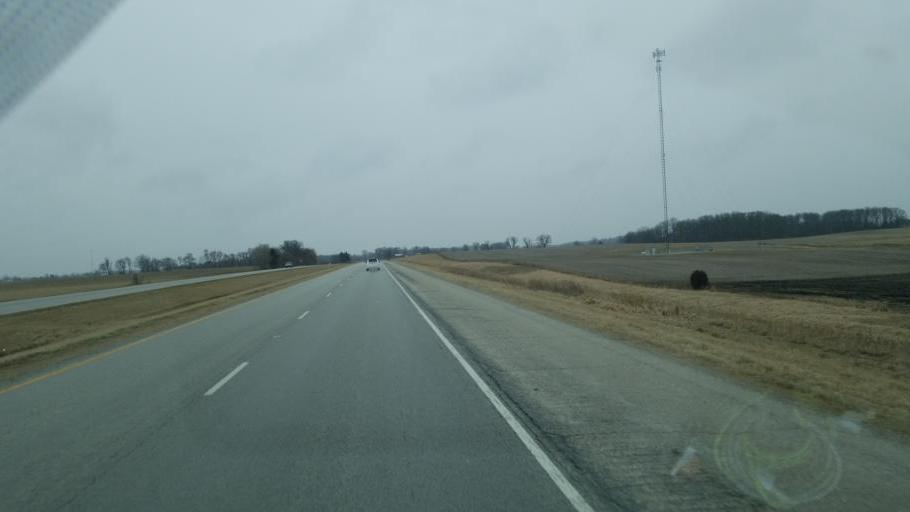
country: US
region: Indiana
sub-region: Fulton County
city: Rochester
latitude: 40.9088
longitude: -86.1595
